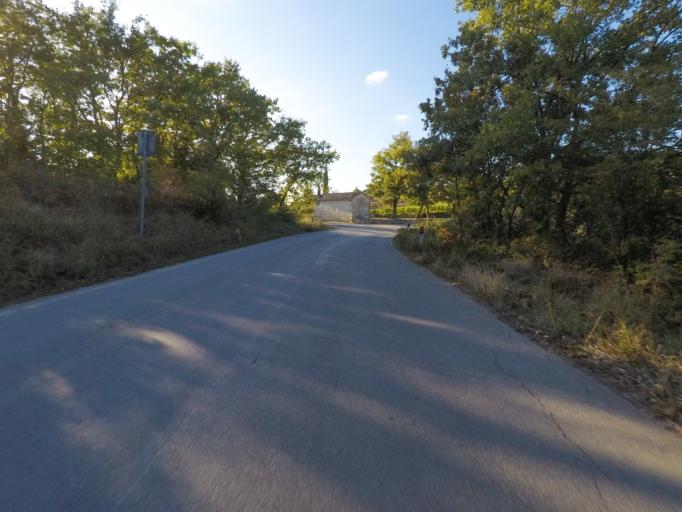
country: IT
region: Tuscany
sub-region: Provincia di Siena
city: Radda in Chianti
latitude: 43.4484
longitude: 11.3916
